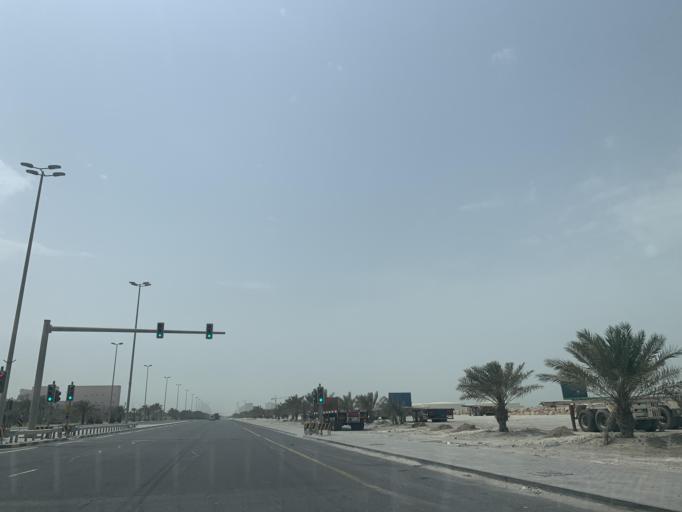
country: BH
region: Muharraq
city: Al Hadd
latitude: 26.2255
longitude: 50.6744
